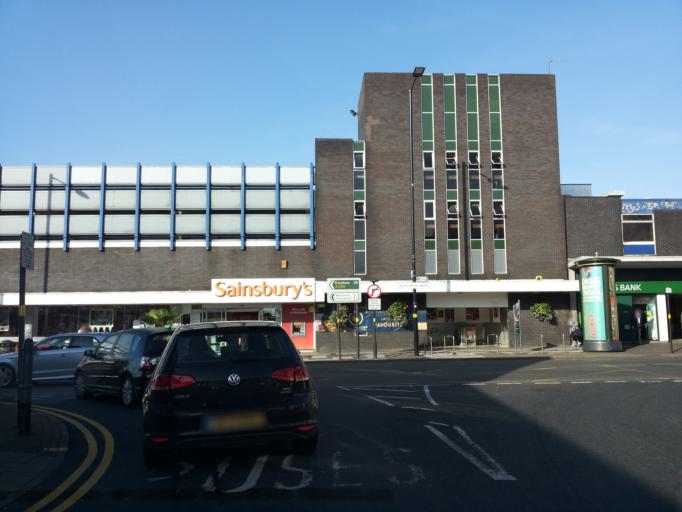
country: GB
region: England
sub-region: City and Borough of Birmingham
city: Birmingham
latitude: 52.4315
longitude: -1.8925
